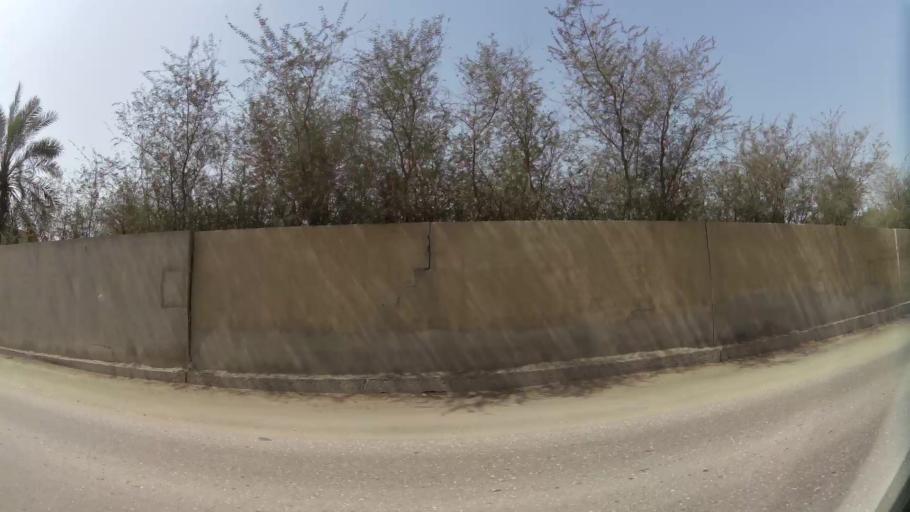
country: BH
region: Manama
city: Jidd Hafs
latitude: 26.2239
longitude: 50.4776
